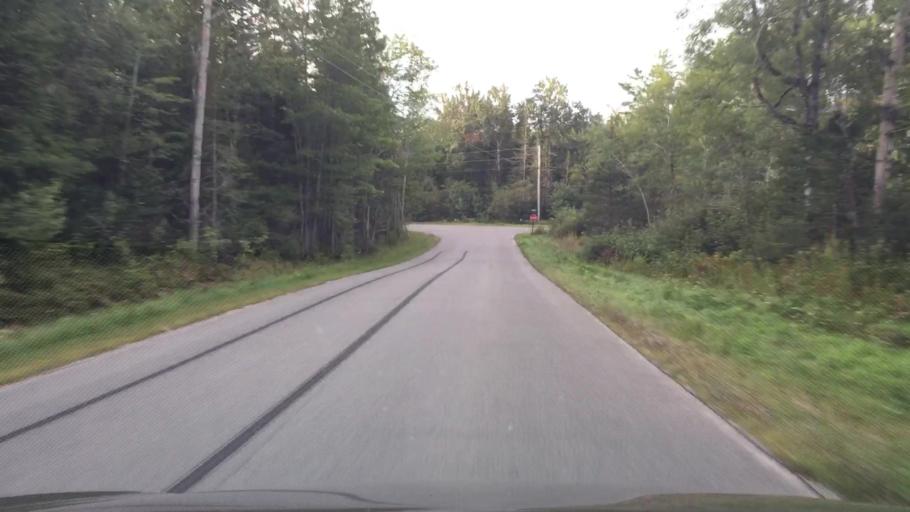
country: US
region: Maine
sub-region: Waldo County
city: Stockton Springs
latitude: 44.4950
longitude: -68.8741
